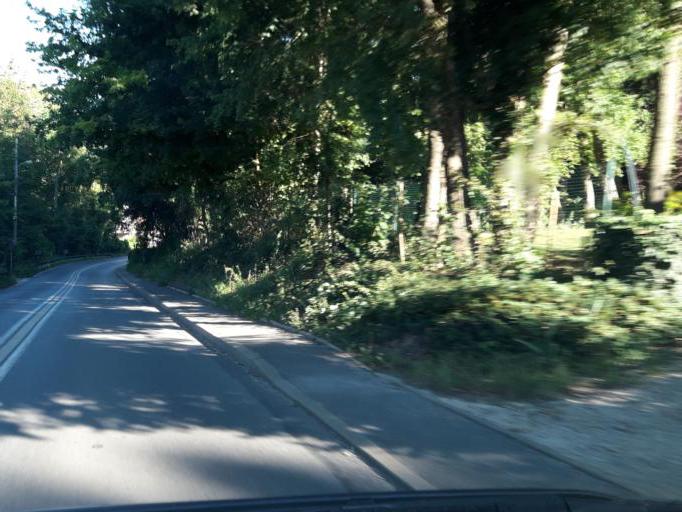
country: FR
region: Ile-de-France
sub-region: Departement de l'Essonne
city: Itteville
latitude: 48.5275
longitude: 2.3441
